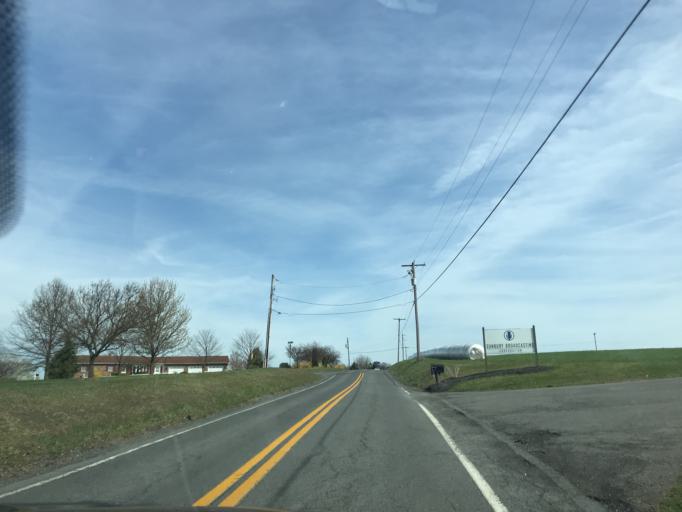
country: US
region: Pennsylvania
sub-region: Northumberland County
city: Northumberland
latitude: 40.8853
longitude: -76.8197
